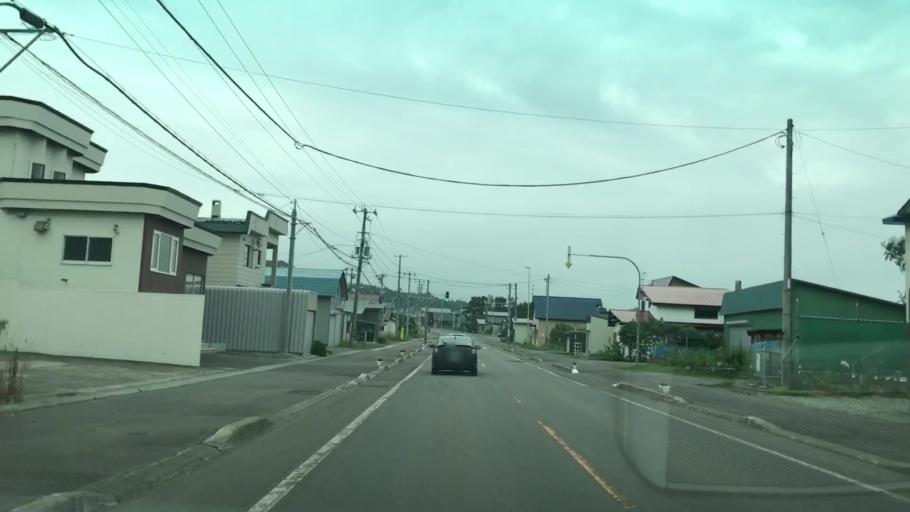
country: JP
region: Hokkaido
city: Iwanai
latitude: 42.7776
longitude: 140.3059
